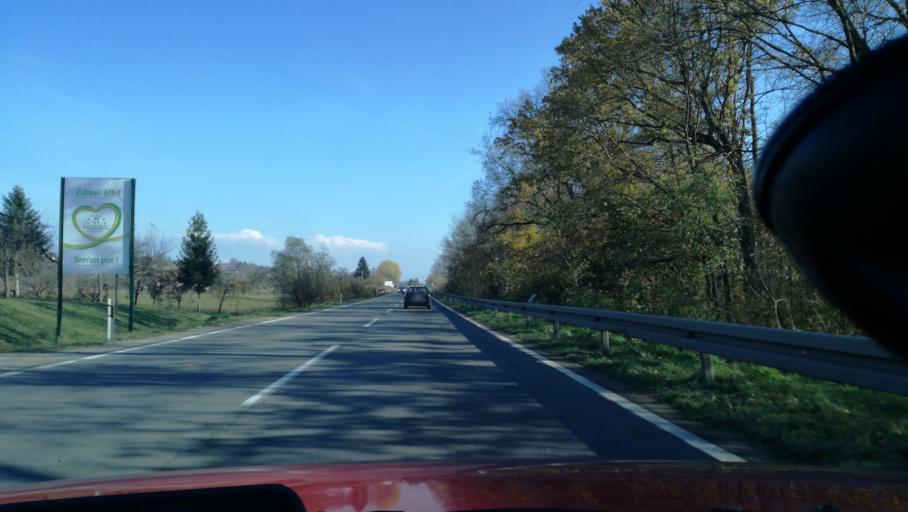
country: RS
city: Prislonica
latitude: 43.8896
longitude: 20.4536
